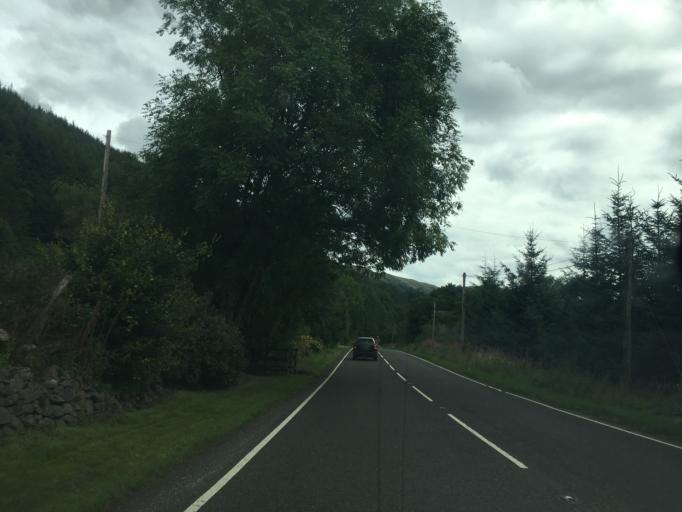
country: GB
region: Scotland
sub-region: Stirling
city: Callander
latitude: 56.3013
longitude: -4.3113
